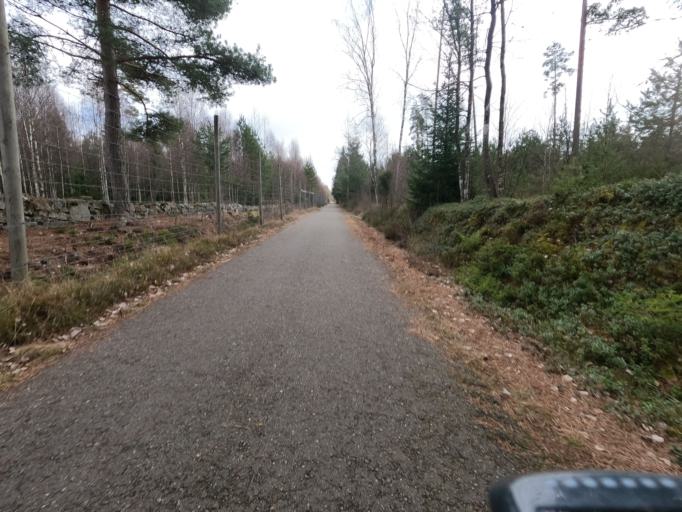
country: SE
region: Joenkoeping
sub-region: Varnamo Kommun
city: Rydaholm
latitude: 56.8577
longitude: 14.1803
